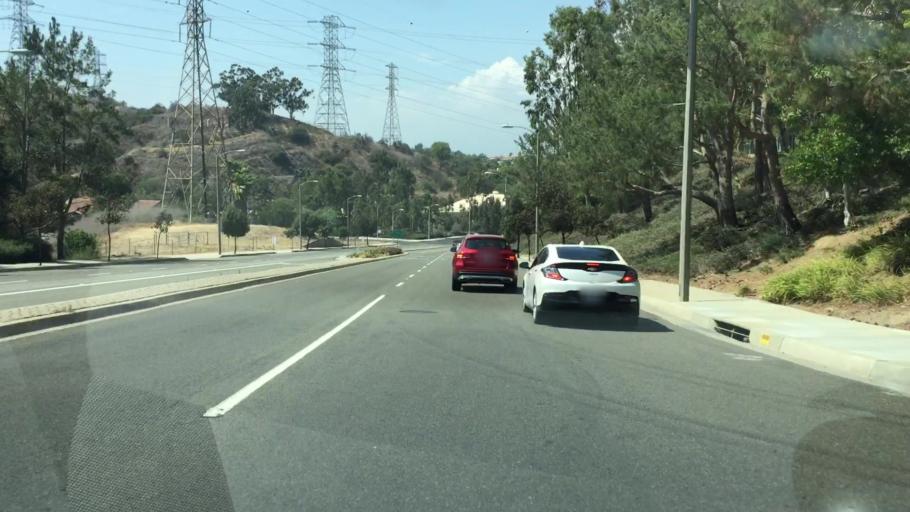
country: US
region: California
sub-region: Los Angeles County
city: Rowland Heights
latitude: 33.9648
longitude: -117.9148
